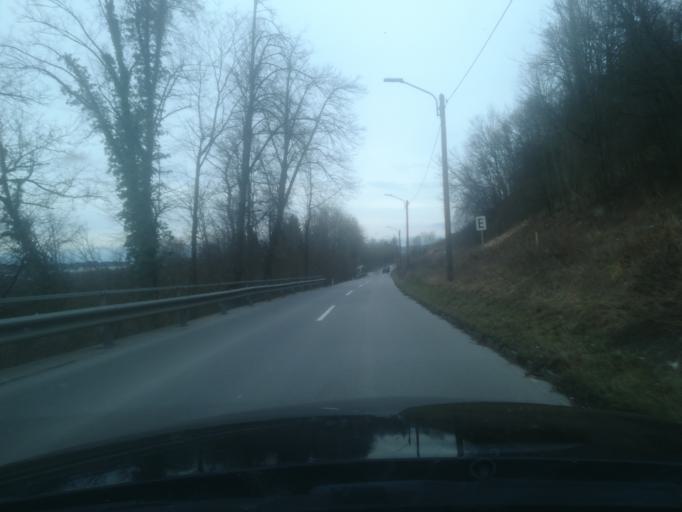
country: AT
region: Upper Austria
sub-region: Wels-Land
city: Steinhaus
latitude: 48.1369
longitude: 14.0083
